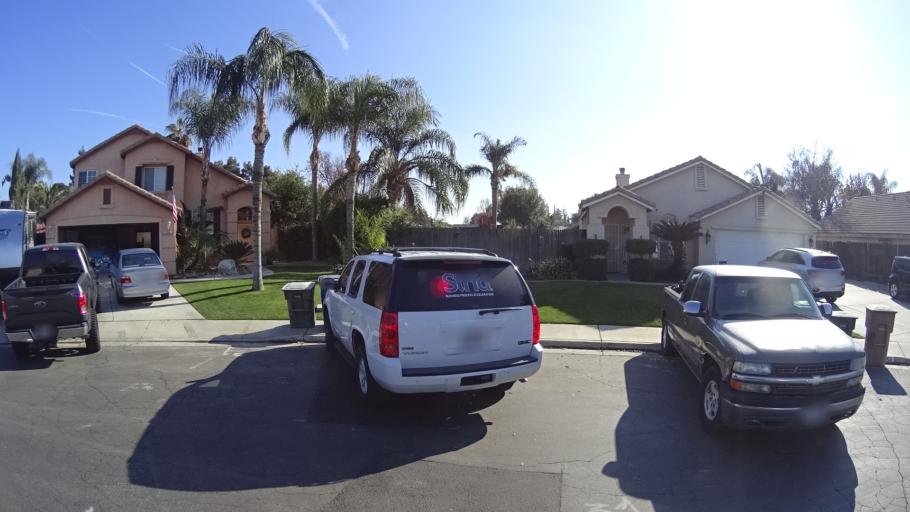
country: US
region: California
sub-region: Kern County
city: Greenacres
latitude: 35.3162
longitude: -119.1076
